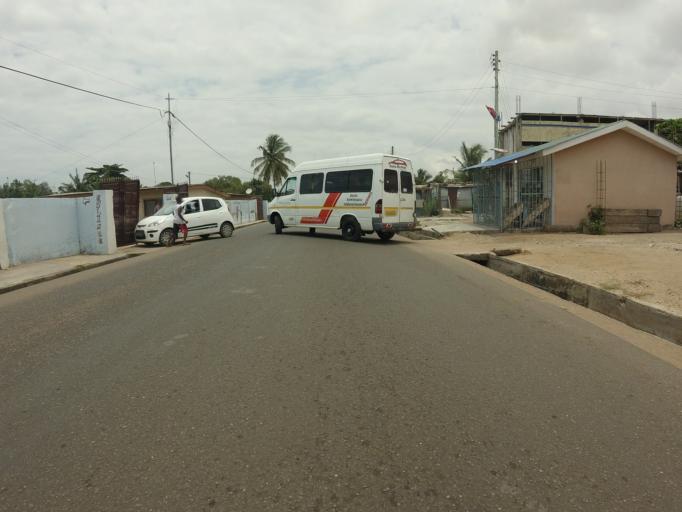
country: GH
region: Greater Accra
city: Nungua
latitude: 5.6176
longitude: -0.0796
